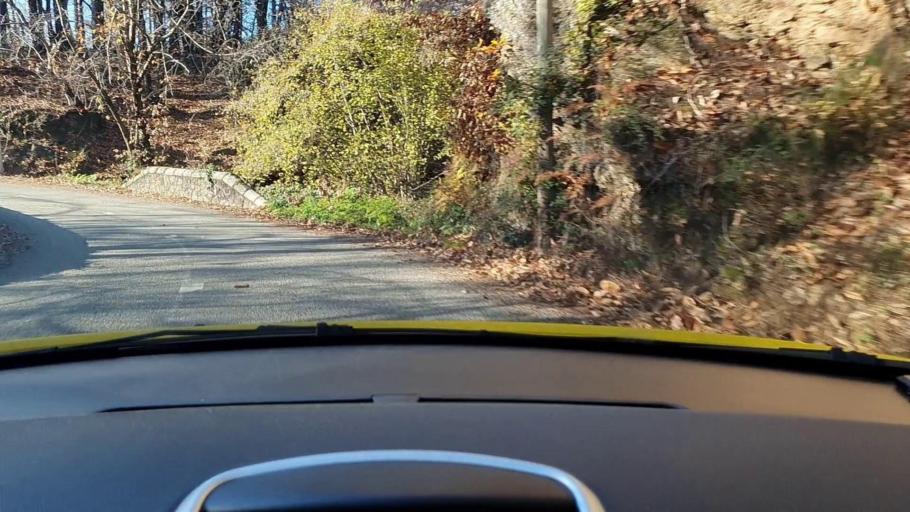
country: FR
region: Languedoc-Roussillon
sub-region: Departement du Gard
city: Branoux-les-Taillades
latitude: 44.2844
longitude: 3.9638
